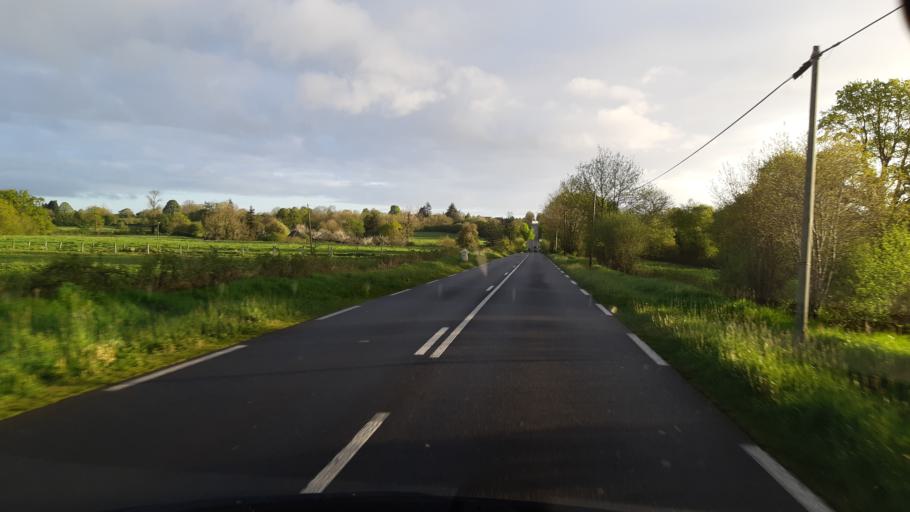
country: FR
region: Lower Normandy
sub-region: Departement de la Manche
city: Tessy-sur-Vire
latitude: 49.0186
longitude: -1.1476
